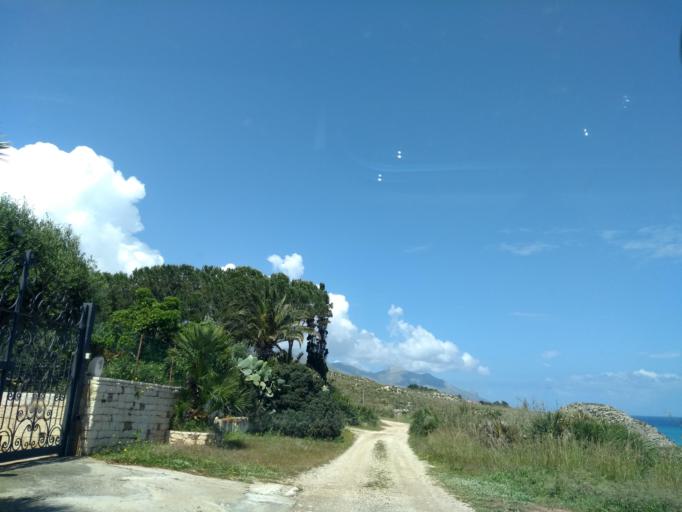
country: IT
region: Sicily
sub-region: Trapani
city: Castellammare del Golfo
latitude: 38.0504
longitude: 12.8527
